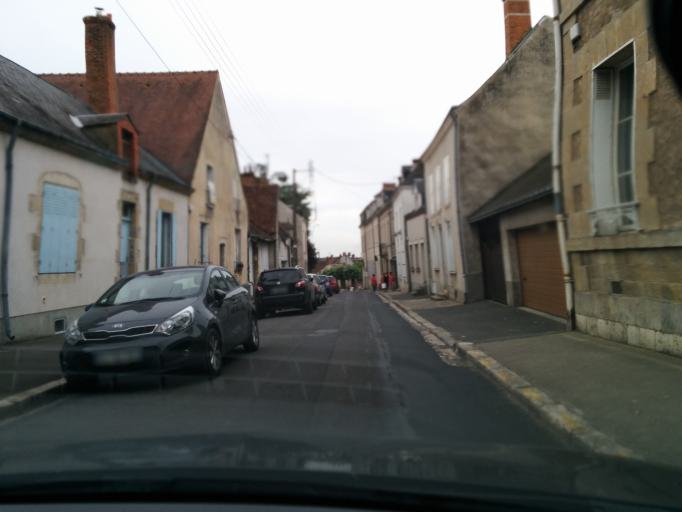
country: FR
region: Centre
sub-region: Departement du Loiret
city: Chateauneuf-sur-Loire
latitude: 47.8628
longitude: 2.2199
